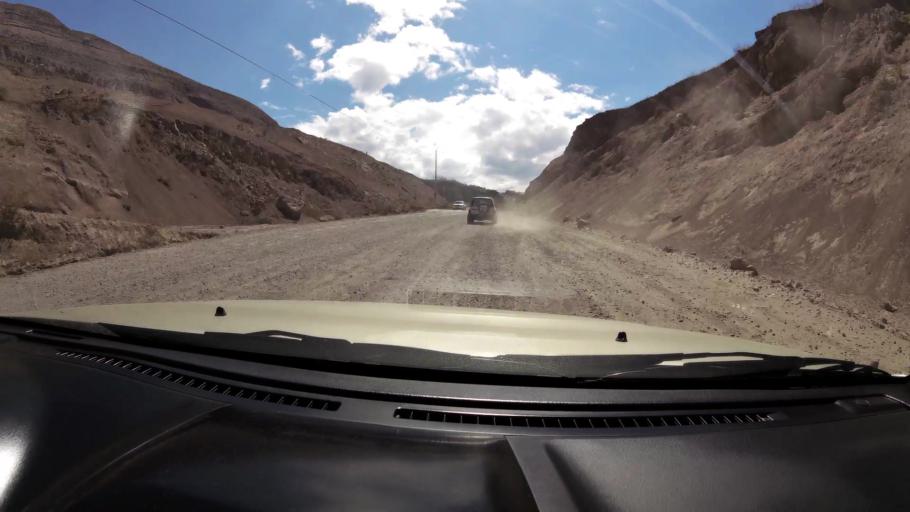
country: EC
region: El Oro
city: Zaruma
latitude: -3.3250
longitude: -79.3552
